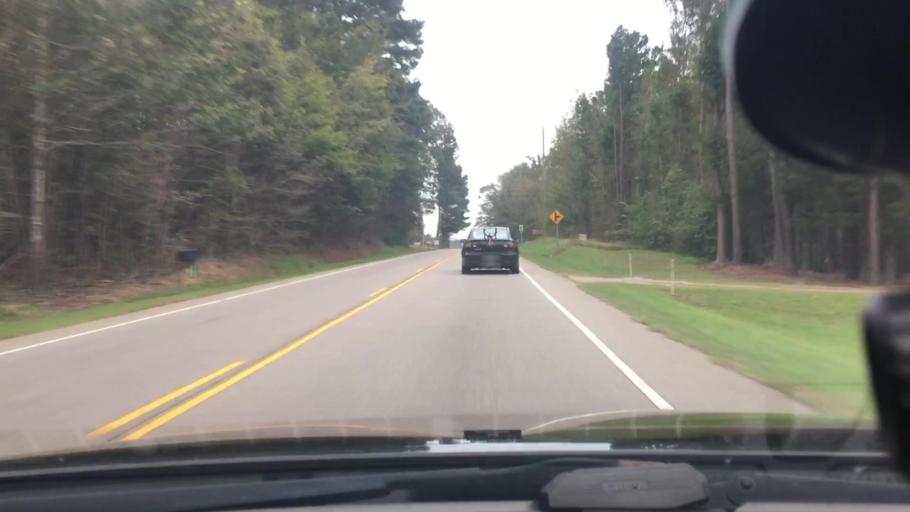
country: US
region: North Carolina
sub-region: Moore County
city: Robbins
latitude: 35.4018
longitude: -79.5563
